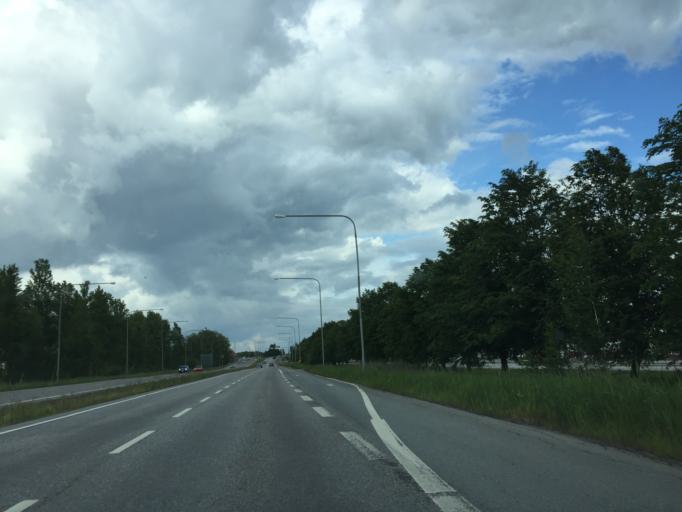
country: SE
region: OErebro
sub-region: Orebro Kommun
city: Orebro
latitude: 59.2641
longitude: 15.1859
